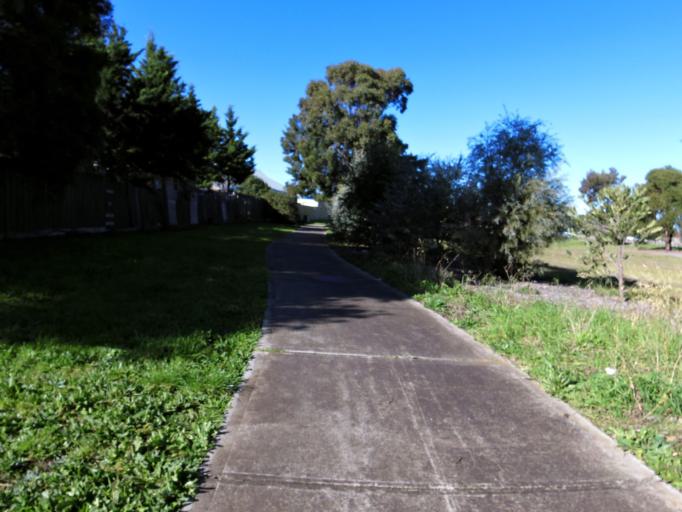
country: AU
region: Victoria
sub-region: Wyndham
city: Tarneit
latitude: -37.8758
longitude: 144.6746
